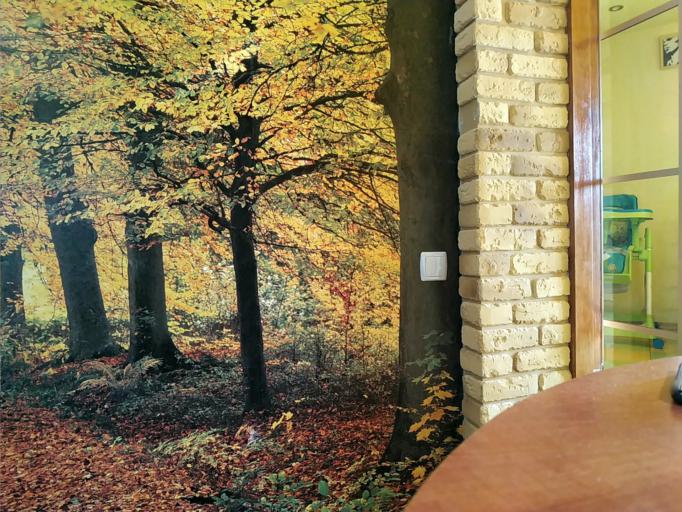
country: RU
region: Novgorod
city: Parfino
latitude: 57.7980
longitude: 31.6218
